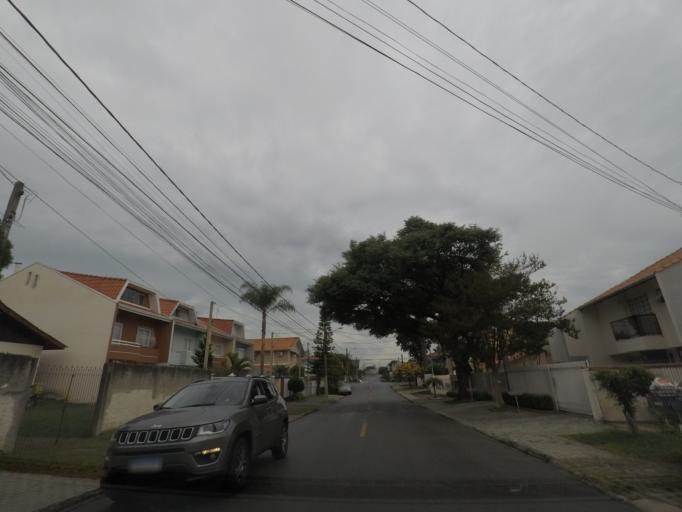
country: BR
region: Parana
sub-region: Curitiba
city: Curitiba
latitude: -25.4714
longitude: -49.3081
